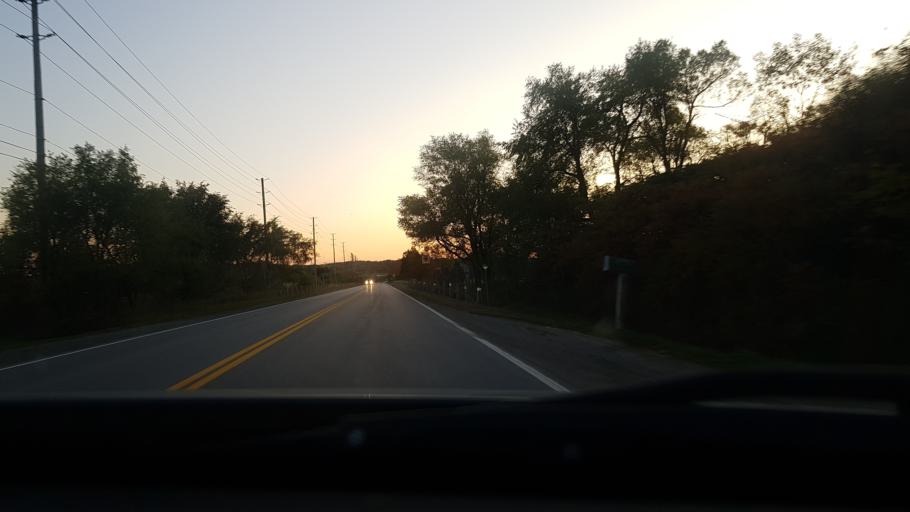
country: CA
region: Ontario
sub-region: Halton
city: Milton
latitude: 43.5042
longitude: -79.9620
